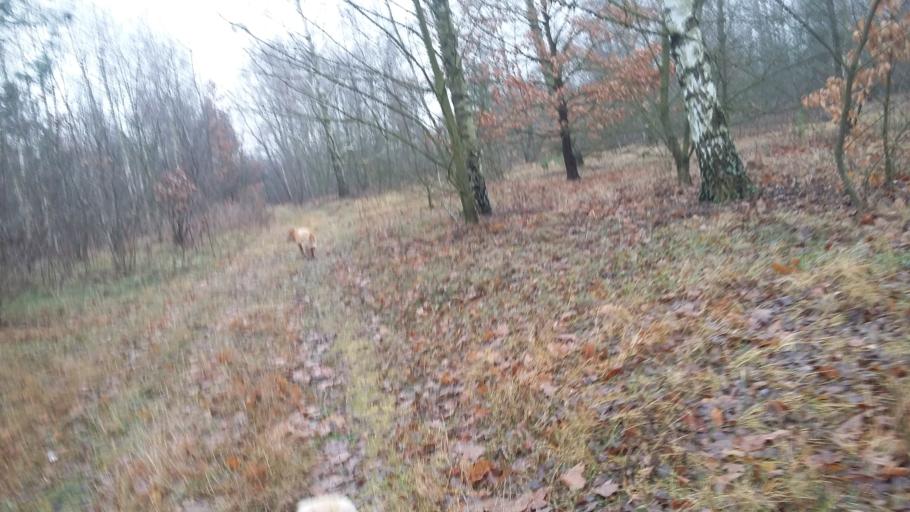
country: PL
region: Lodz Voivodeship
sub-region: Powiat pabianicki
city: Ksawerow
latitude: 51.7299
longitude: 19.4097
